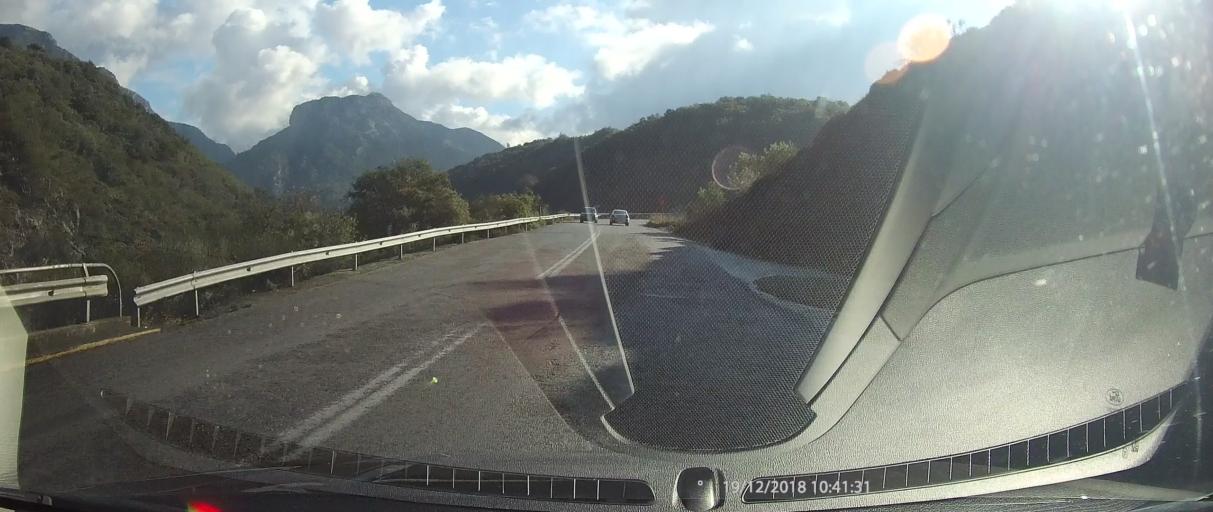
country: GR
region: Peloponnese
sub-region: Nomos Messinias
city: Paralia Vergas
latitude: 36.9552
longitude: 22.1924
